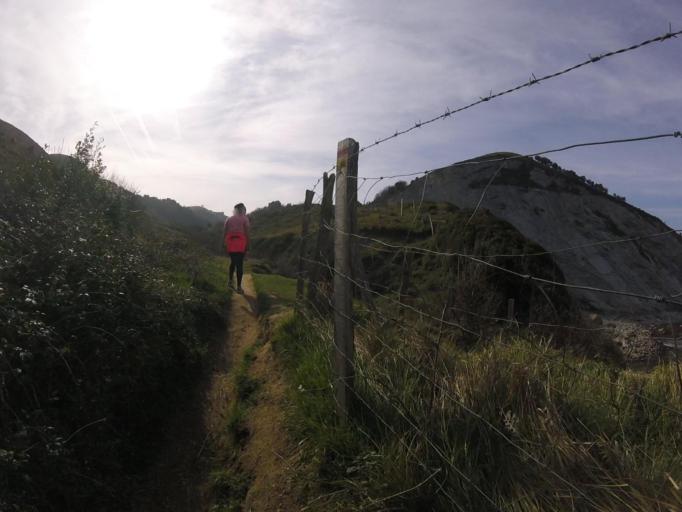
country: ES
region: Basque Country
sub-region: Provincia de Guipuzcoa
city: Deba
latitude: 43.2964
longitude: -2.3165
